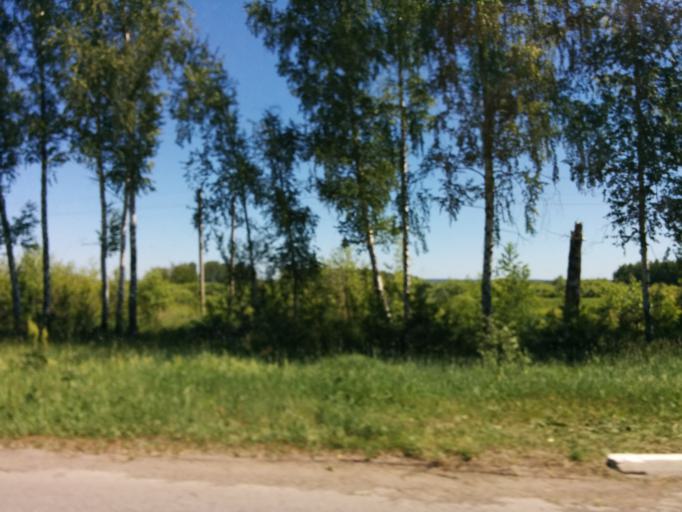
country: RU
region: Tambov
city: Goreloye
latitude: 53.0059
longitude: 41.4634
